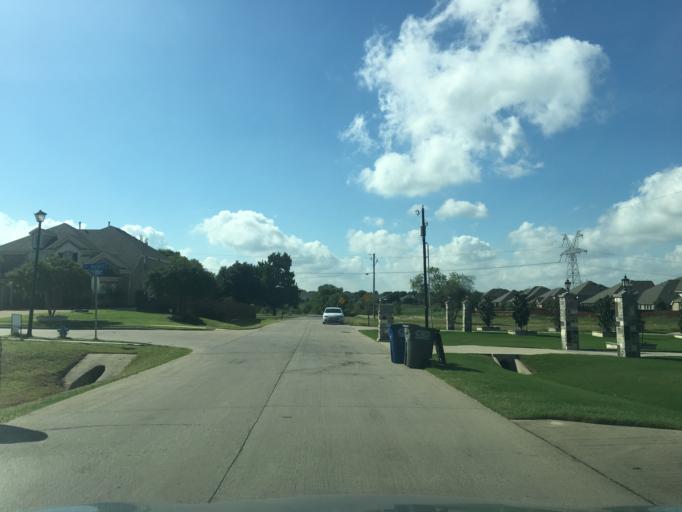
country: US
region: Texas
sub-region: Dallas County
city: Sachse
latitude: 32.9699
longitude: -96.5791
